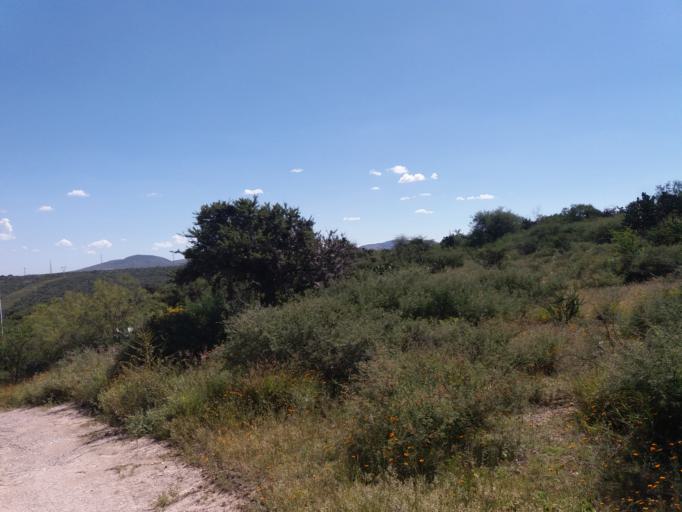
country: MX
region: Aguascalientes
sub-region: Aguascalientes
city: Villa Licenciado Jesus Teran (Calvillito)
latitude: 21.7820
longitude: -102.2262
